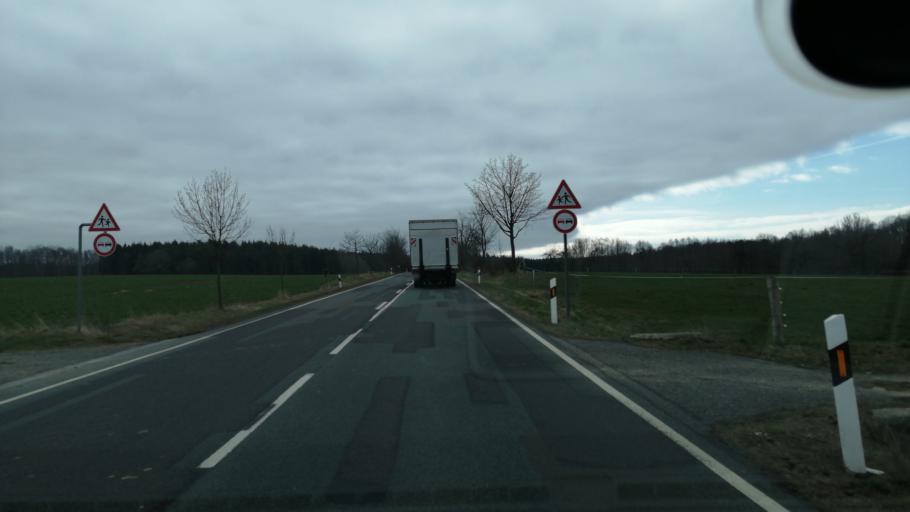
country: DE
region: Saxony
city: Niedercunnersdorf
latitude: 51.0551
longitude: 14.6982
